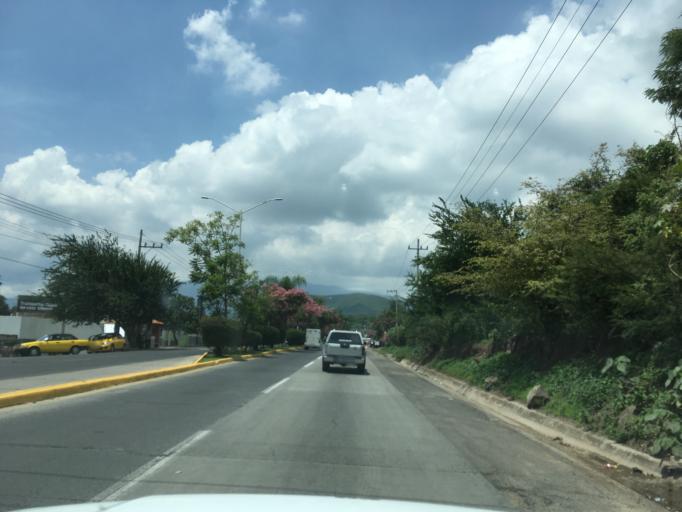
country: MX
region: Jalisco
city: Tlajomulco de Zuniga
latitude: 20.4757
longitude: -103.4523
